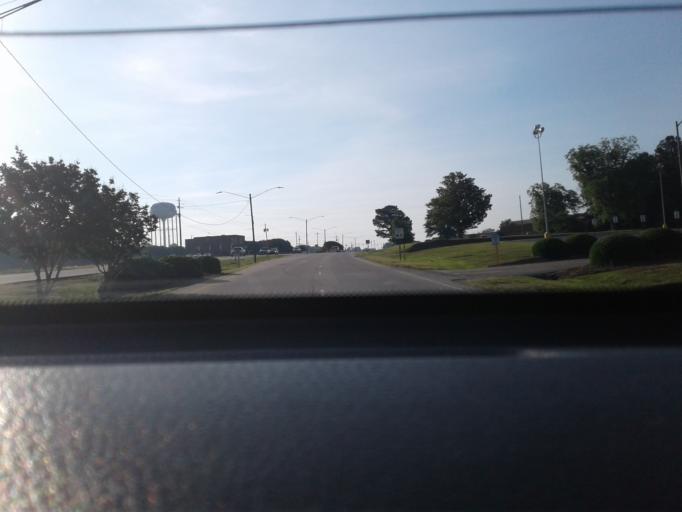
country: US
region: North Carolina
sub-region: Harnett County
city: Dunn
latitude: 35.3205
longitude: -78.6346
